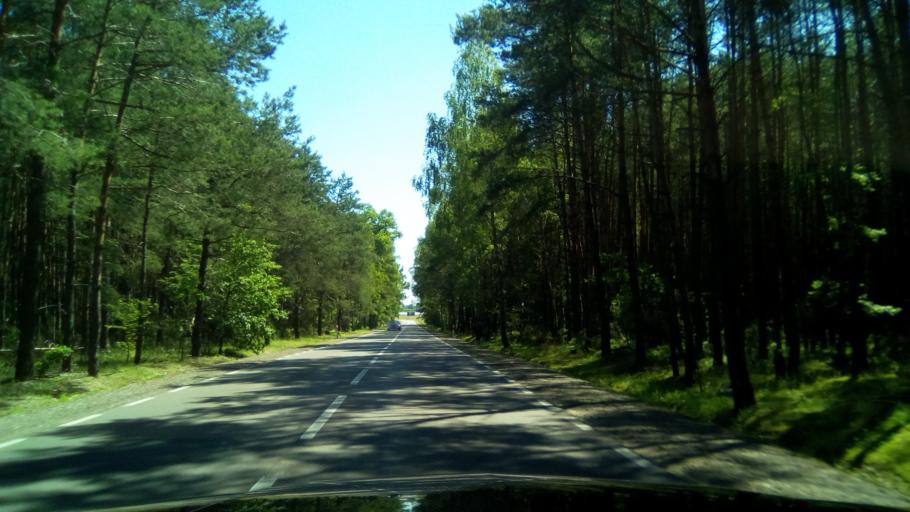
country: PL
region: Masovian Voivodeship
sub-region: Powiat przysuski
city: Klwow
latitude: 51.5288
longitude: 20.6088
